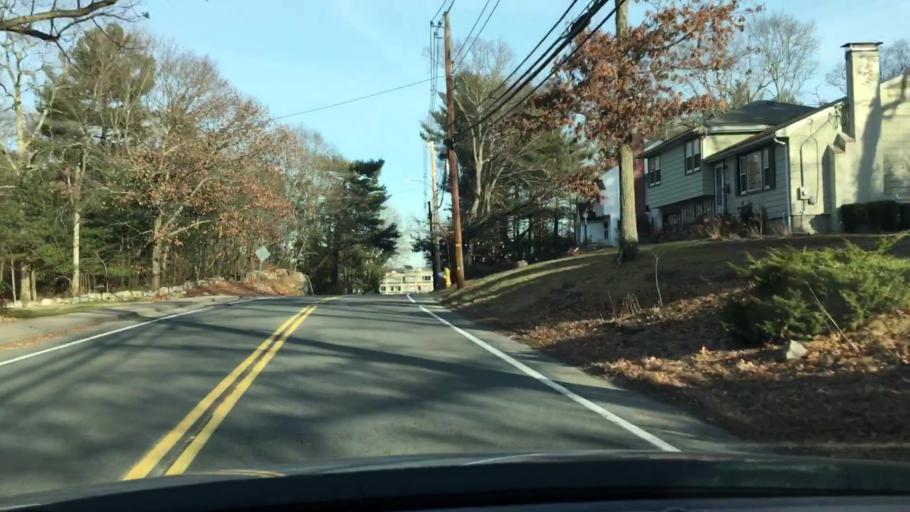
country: US
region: Massachusetts
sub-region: Norfolk County
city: Dedham
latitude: 42.2278
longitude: -71.1888
